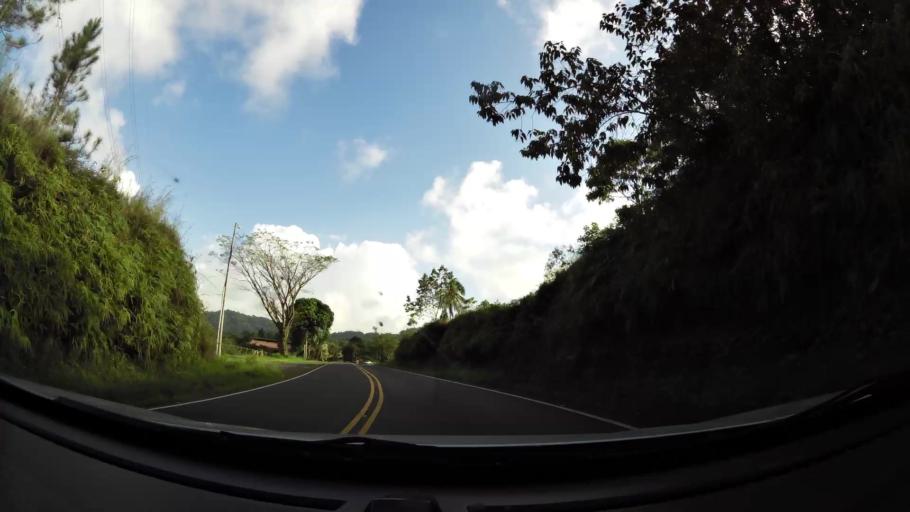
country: CR
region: Limon
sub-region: Canton de Siquirres
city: Siquirres
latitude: 10.0642
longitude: -83.5535
